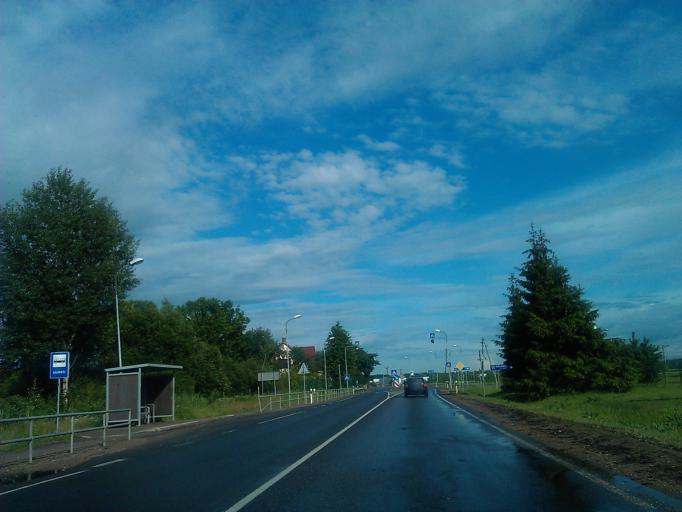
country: LV
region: Salaspils
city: Salaspils
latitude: 56.9131
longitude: 24.3632
